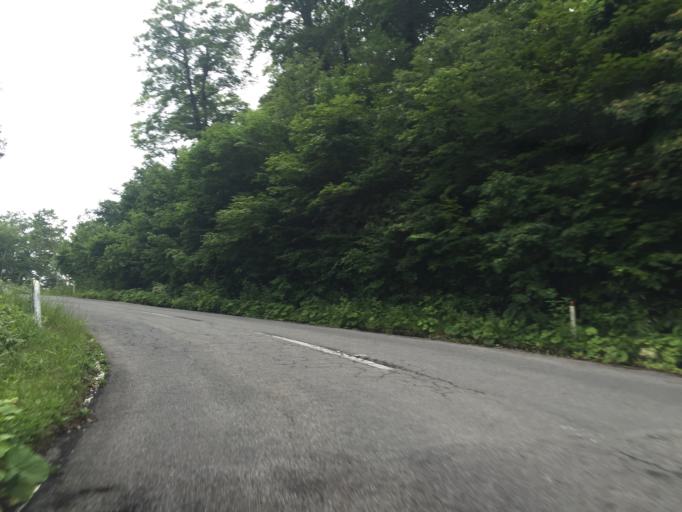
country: JP
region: Yamagata
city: Yonezawa
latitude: 37.7505
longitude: 140.1012
